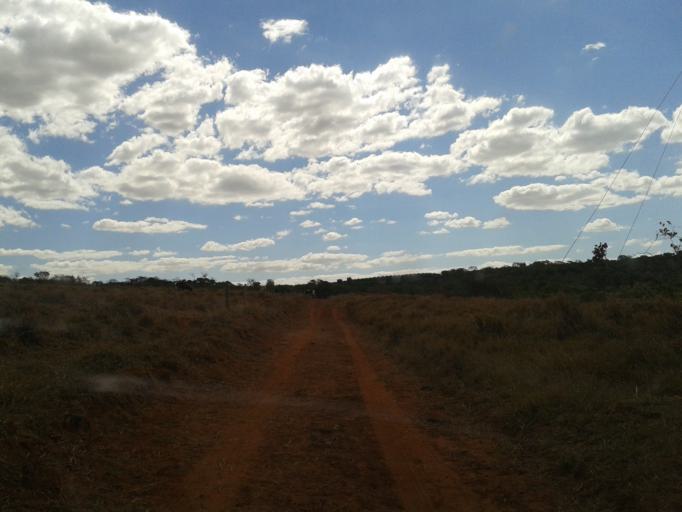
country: BR
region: Minas Gerais
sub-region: Centralina
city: Centralina
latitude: -18.7895
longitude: -49.0971
